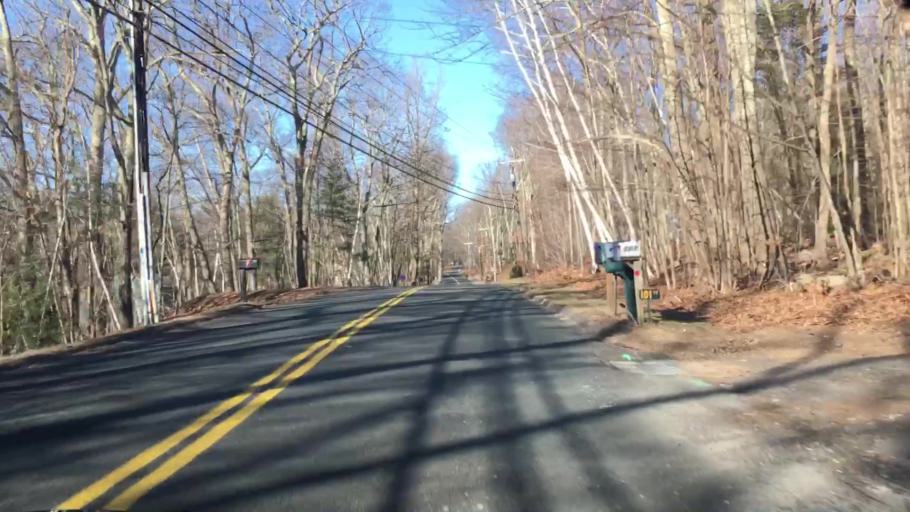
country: US
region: Connecticut
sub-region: Tolland County
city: Crystal Lake
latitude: 41.9366
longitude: -72.3885
